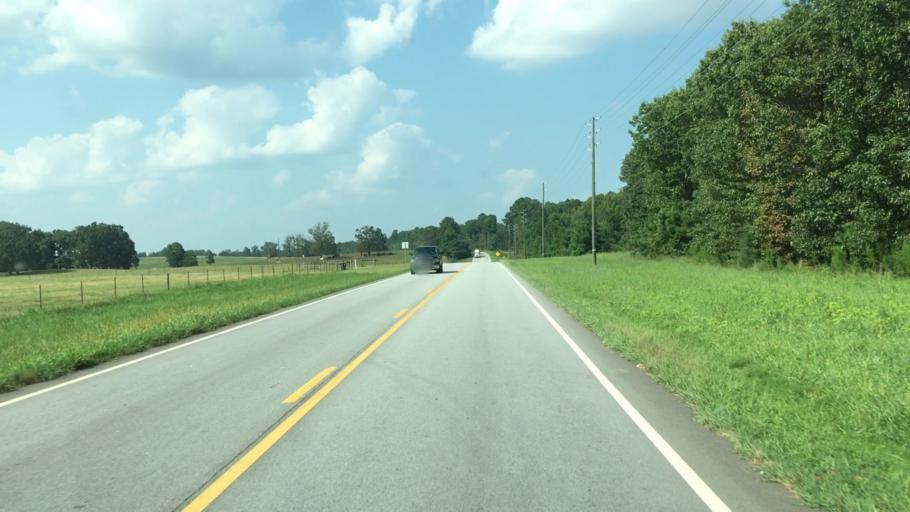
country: US
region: Georgia
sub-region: Jasper County
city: Monticello
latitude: 33.4506
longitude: -83.7547
